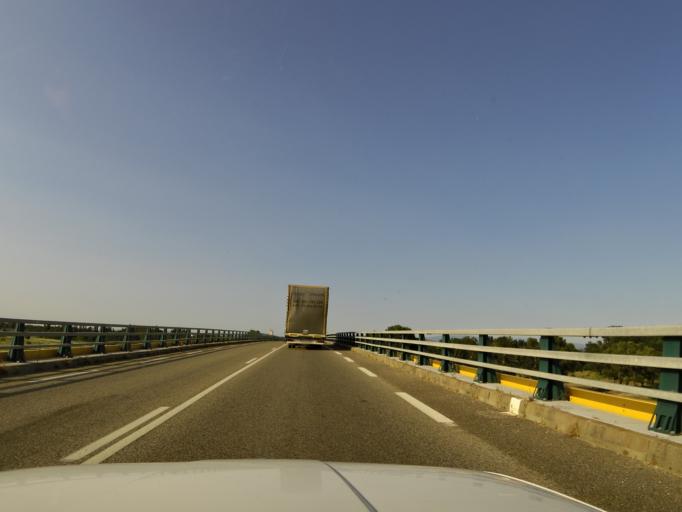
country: FR
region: Languedoc-Roussillon
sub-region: Departement du Gard
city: Pont-Saint-Esprit
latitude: 44.2523
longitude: 4.6559
